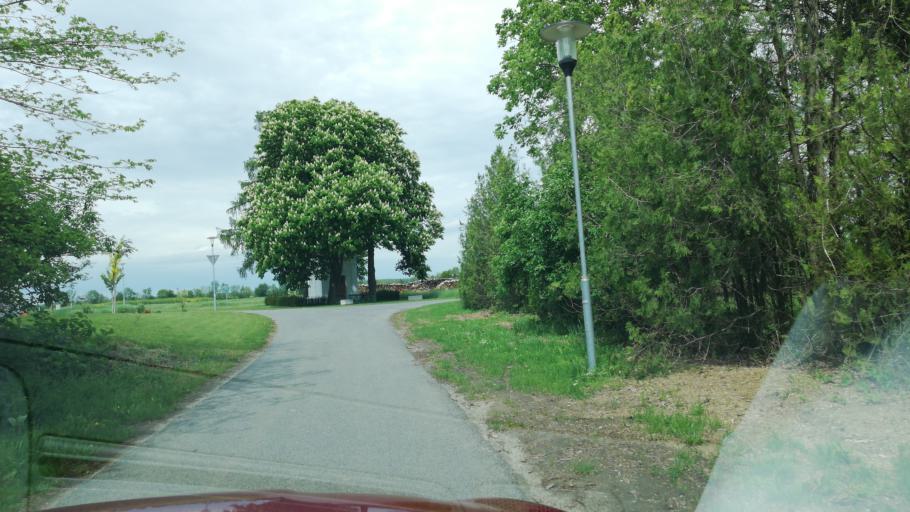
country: AT
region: Burgenland
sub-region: Politischer Bezirk Oberpullendorf
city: Lutzmannsburg
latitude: 47.4559
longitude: 16.6122
